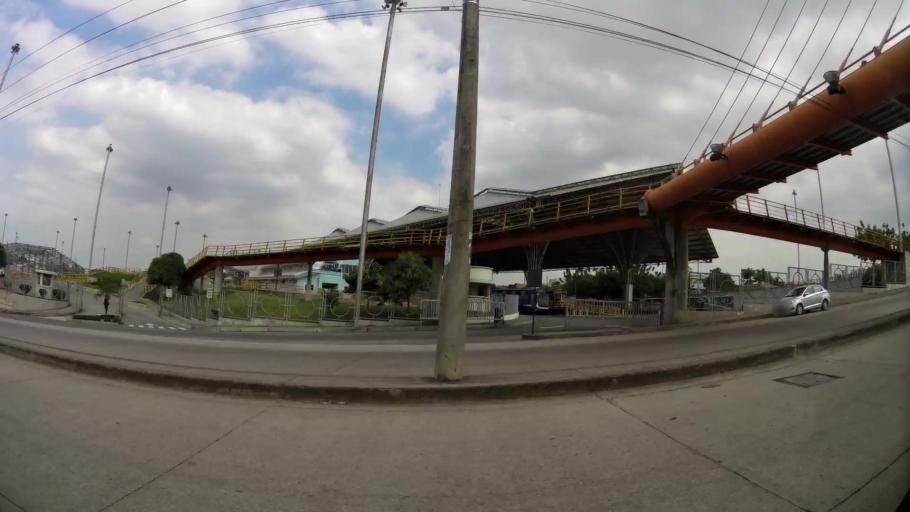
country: EC
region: Guayas
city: Santa Lucia
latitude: -2.0917
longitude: -79.9403
